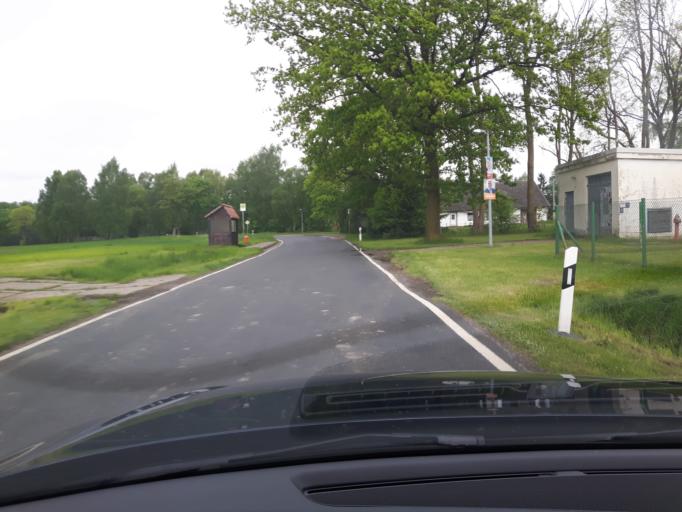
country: DE
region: Mecklenburg-Vorpommern
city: Tribsees
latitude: 54.1915
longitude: 12.7398
